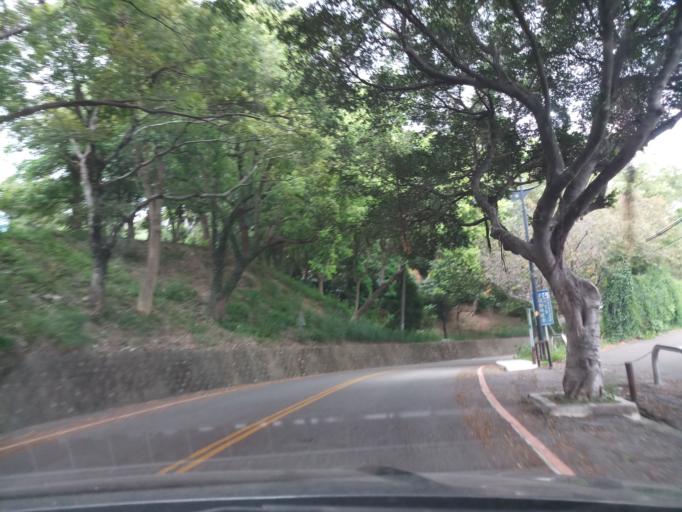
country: TW
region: Taiwan
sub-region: Miaoli
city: Miaoli
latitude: 24.5549
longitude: 120.8081
